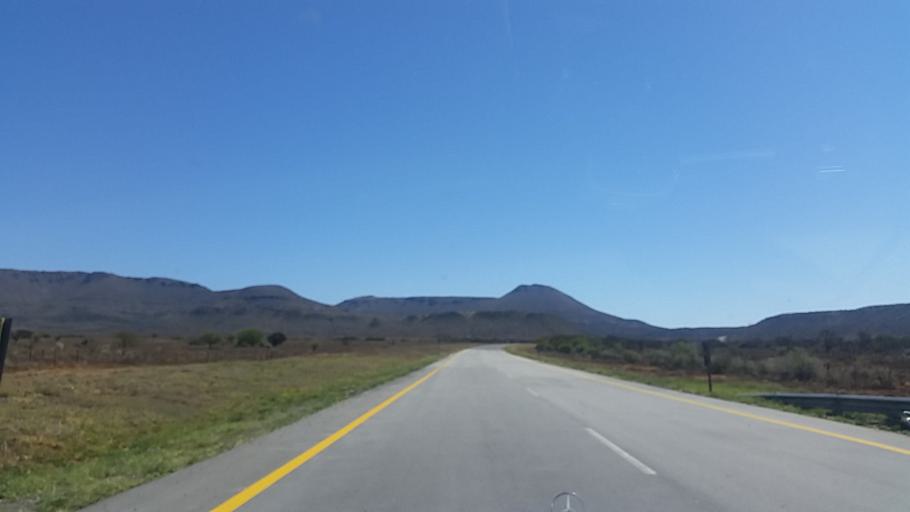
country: ZA
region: Eastern Cape
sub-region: Cacadu District Municipality
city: Graaff-Reinet
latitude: -32.0858
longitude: 24.6024
